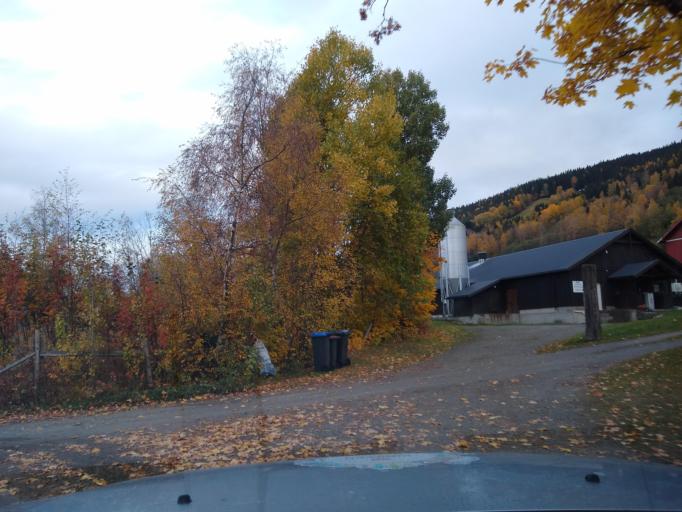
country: NO
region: Oppland
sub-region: Ringebu
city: Ringebu
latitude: 61.5456
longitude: 10.1223
